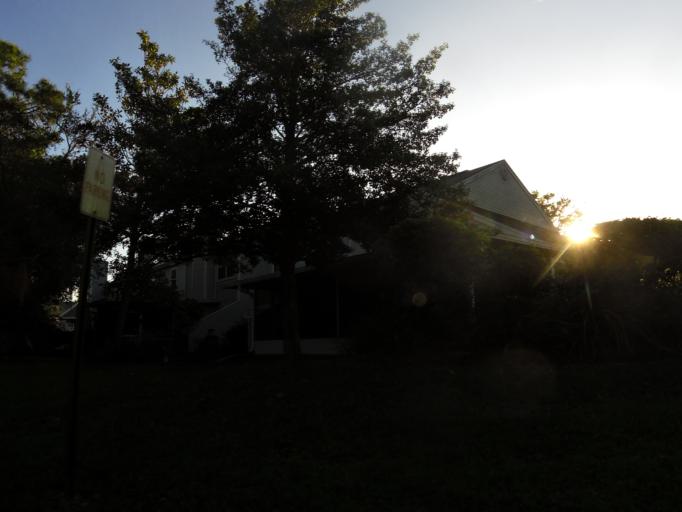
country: US
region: Florida
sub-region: Duval County
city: Atlantic Beach
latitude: 30.3228
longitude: -81.4164
